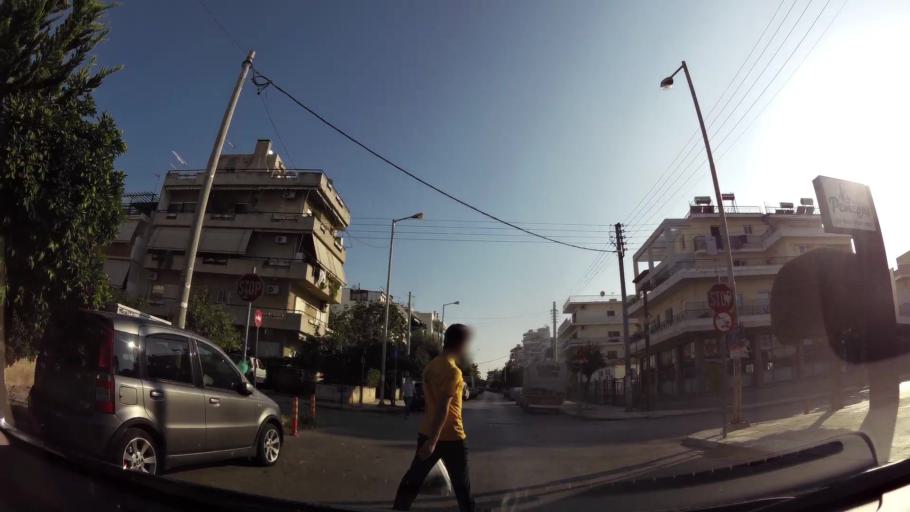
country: GR
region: Attica
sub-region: Nomarchia Athinas
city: Argyroupoli
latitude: 37.9003
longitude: 23.7524
